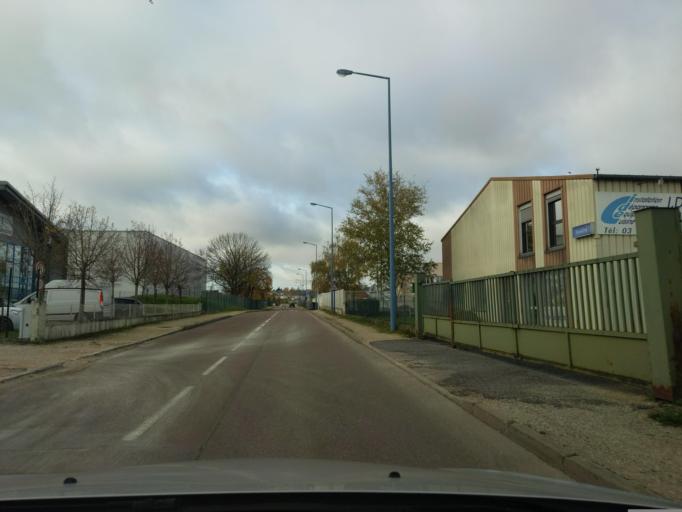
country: FR
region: Bourgogne
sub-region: Departement de la Cote-d'Or
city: Saint-Apollinaire
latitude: 47.3165
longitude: 5.0930
